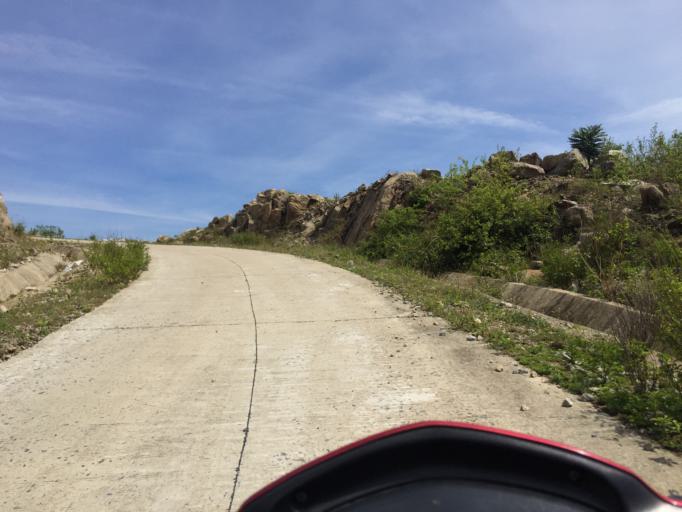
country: VN
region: Quang Nam
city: Hoi An
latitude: 15.9643
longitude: 108.5102
